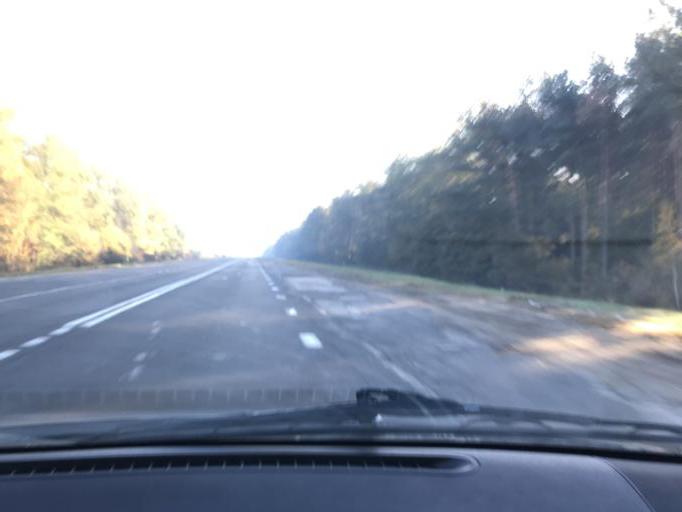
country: BY
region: Brest
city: Asnyezhytsy
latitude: 52.2627
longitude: 26.3216
